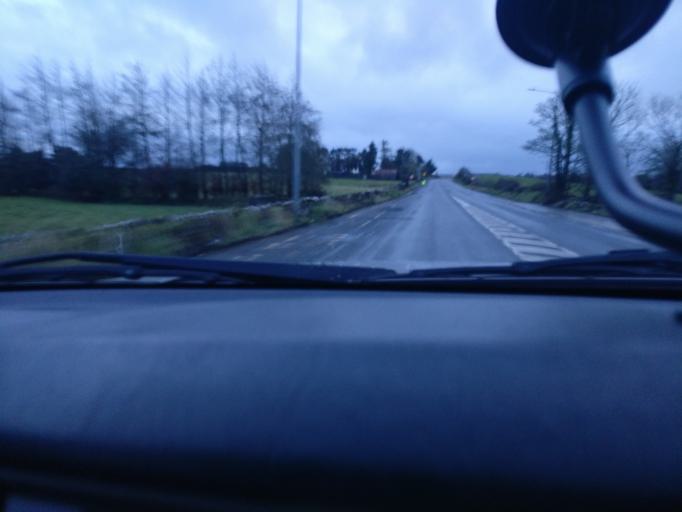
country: IE
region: Connaught
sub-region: County Galway
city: Loughrea
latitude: 53.2266
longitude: -8.4546
